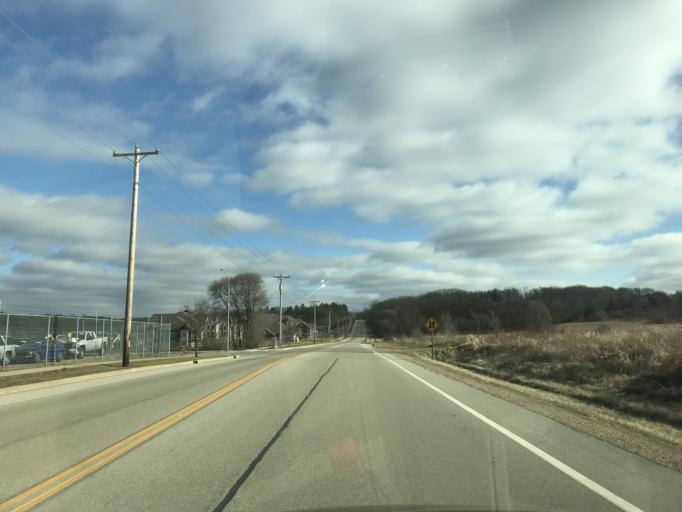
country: US
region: Wisconsin
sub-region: Dane County
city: Monona
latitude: 43.1215
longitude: -89.2867
